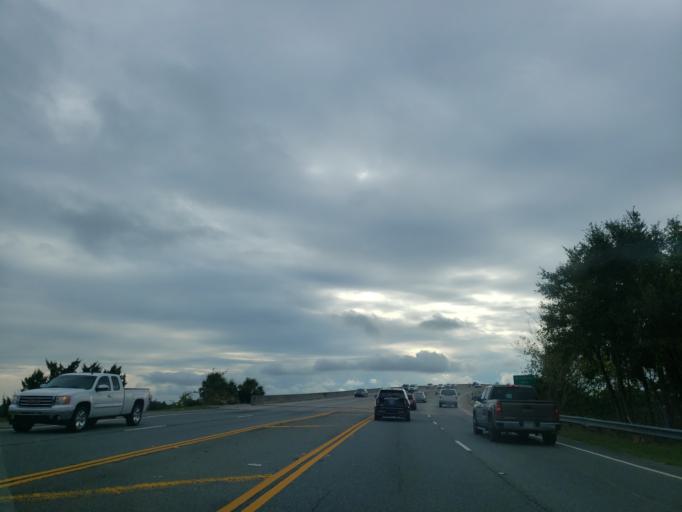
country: US
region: Georgia
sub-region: Chatham County
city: Thunderbolt
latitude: 32.0346
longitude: -81.0415
